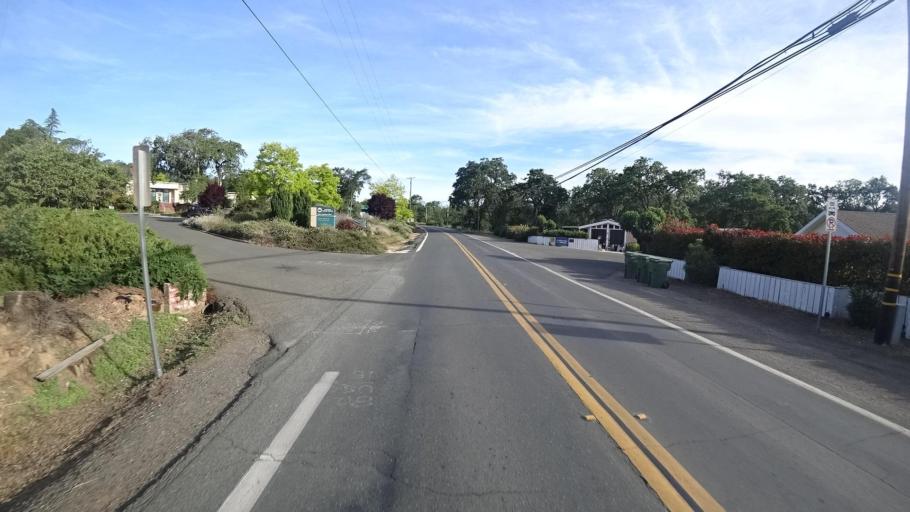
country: US
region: California
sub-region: Lake County
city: North Lakeport
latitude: 39.1052
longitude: -122.9028
